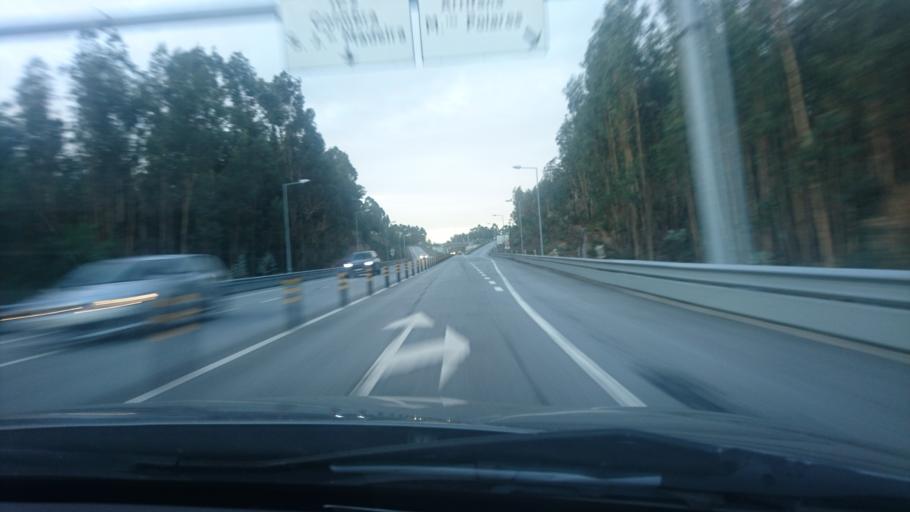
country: PT
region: Aveiro
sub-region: Santa Maria da Feira
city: Arrifana
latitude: 40.9274
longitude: -8.4847
